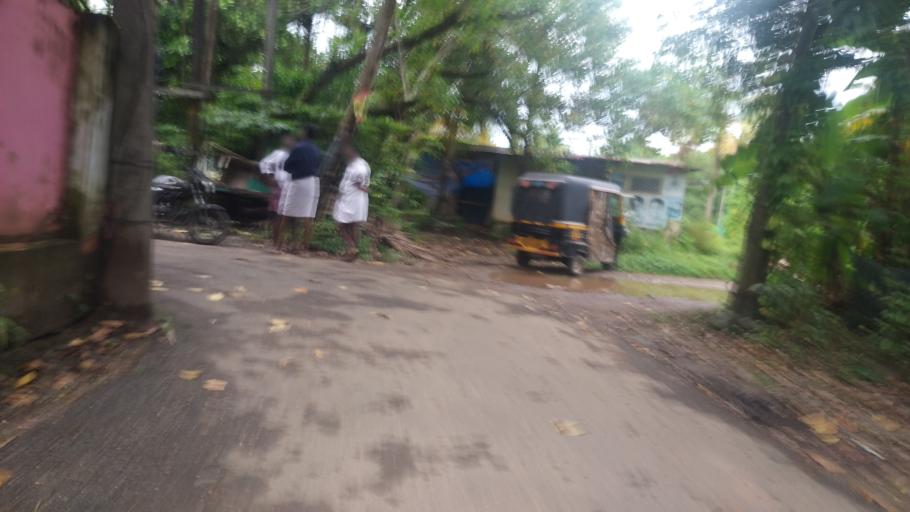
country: IN
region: Kerala
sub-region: Alappuzha
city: Arukutti
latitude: 9.8723
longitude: 76.2856
